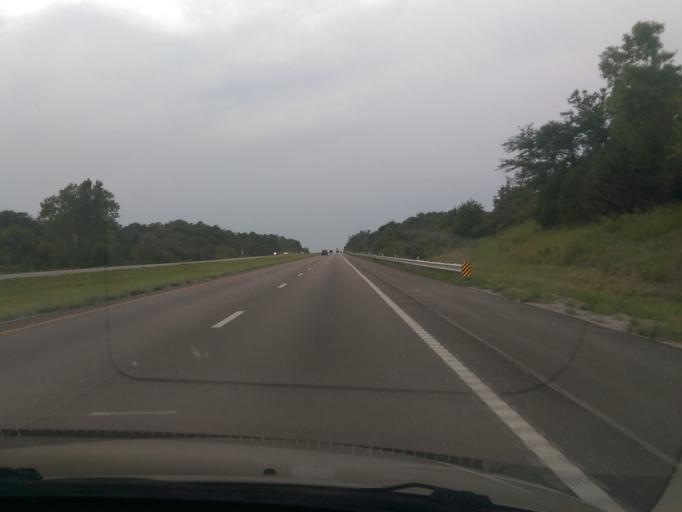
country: US
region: Missouri
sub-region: Andrew County
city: Savannah
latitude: 39.9396
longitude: -94.9354
